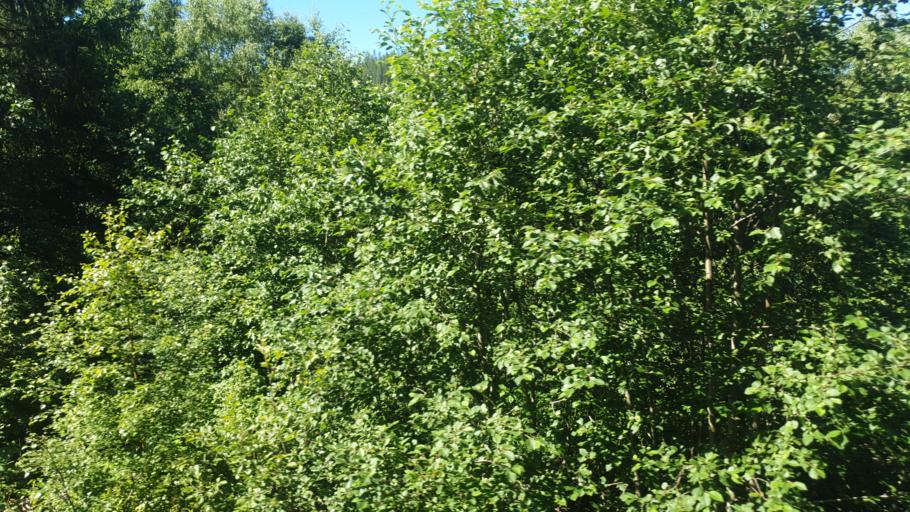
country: NO
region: Sor-Trondelag
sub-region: Meldal
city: Meldal
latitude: 63.1490
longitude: 9.7177
